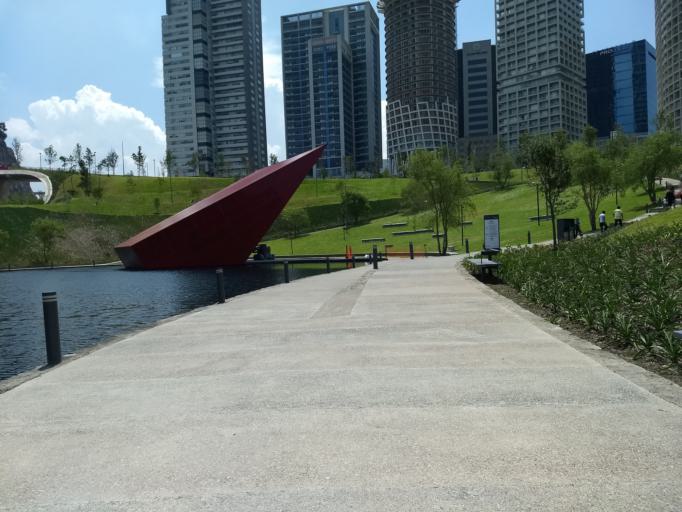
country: MX
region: Mexico City
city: Cuajimalpa
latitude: 19.3554
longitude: -99.2726
